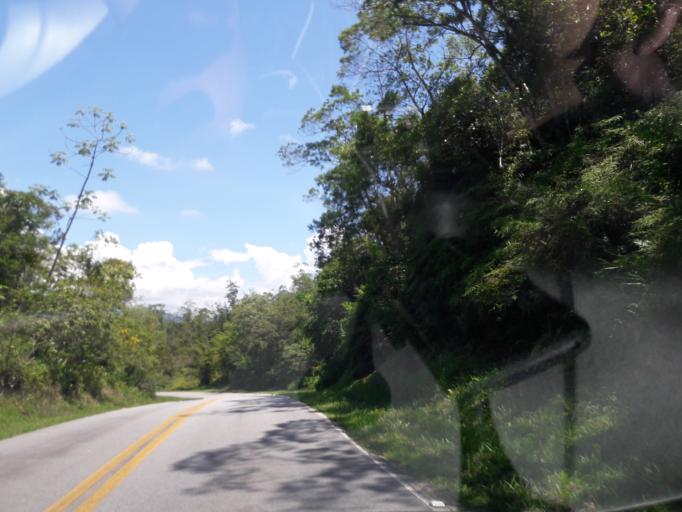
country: BR
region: Parana
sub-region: Antonina
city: Antonina
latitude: -25.5244
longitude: -48.7727
